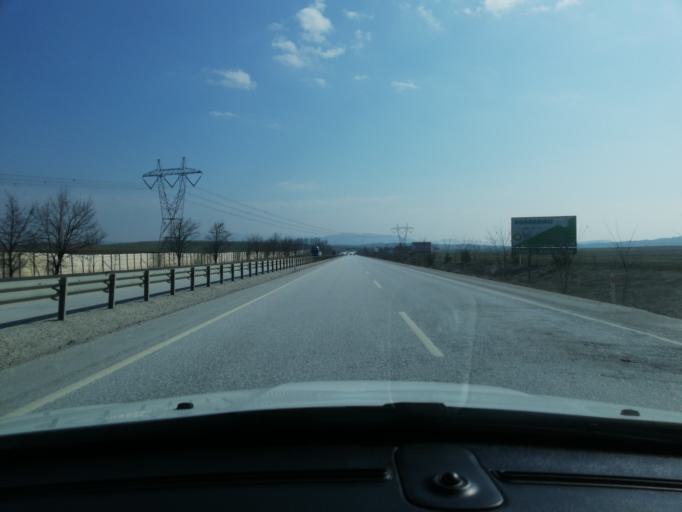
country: TR
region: Cankiri
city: Atkaracalar
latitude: 40.8367
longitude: 33.1533
